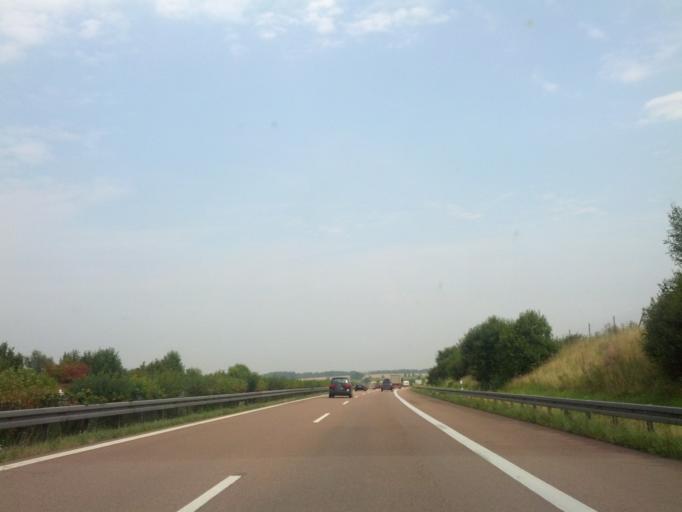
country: DE
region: Mecklenburg-Vorpommern
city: Broderstorf
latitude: 54.0352
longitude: 12.3080
